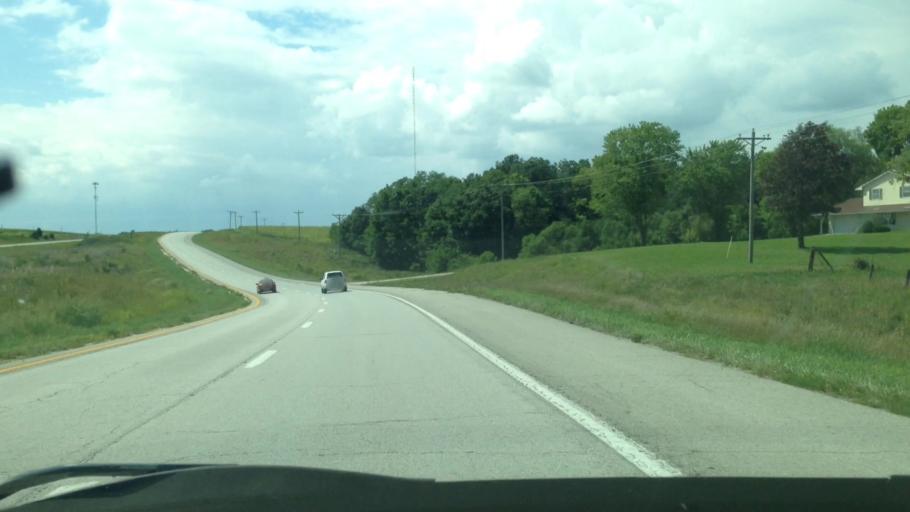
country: US
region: Missouri
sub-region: Pike County
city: Bowling Green
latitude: 39.2598
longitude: -91.0597
